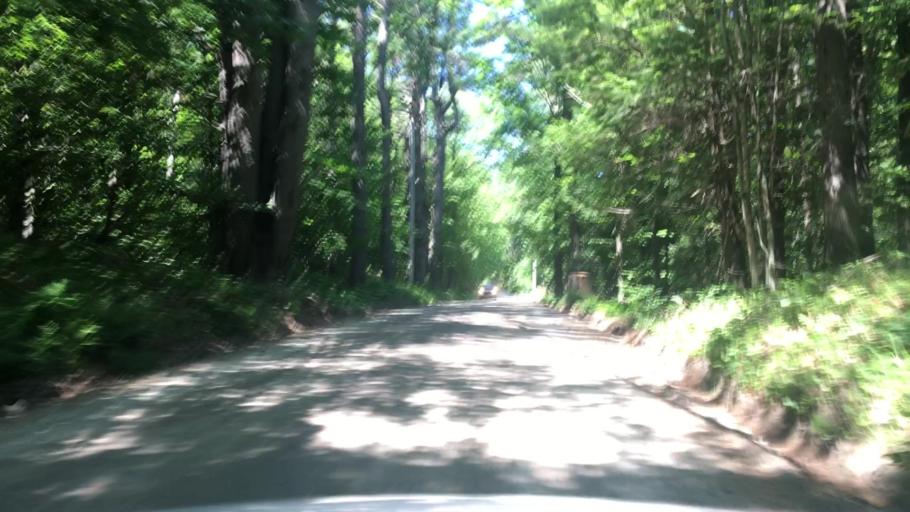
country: US
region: New Hampshire
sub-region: Merrimack County
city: Hopkinton
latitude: 43.2288
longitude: -71.6661
